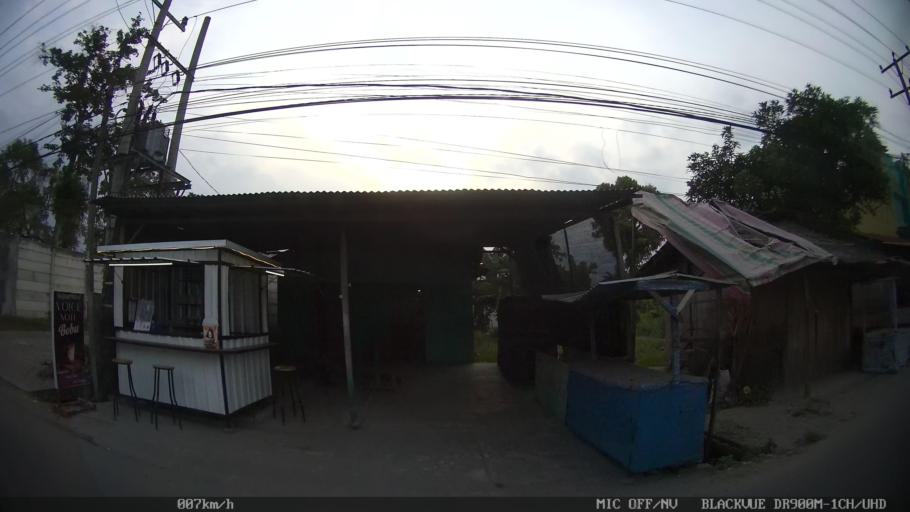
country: ID
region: North Sumatra
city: Sunggal
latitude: 3.5906
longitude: 98.6018
